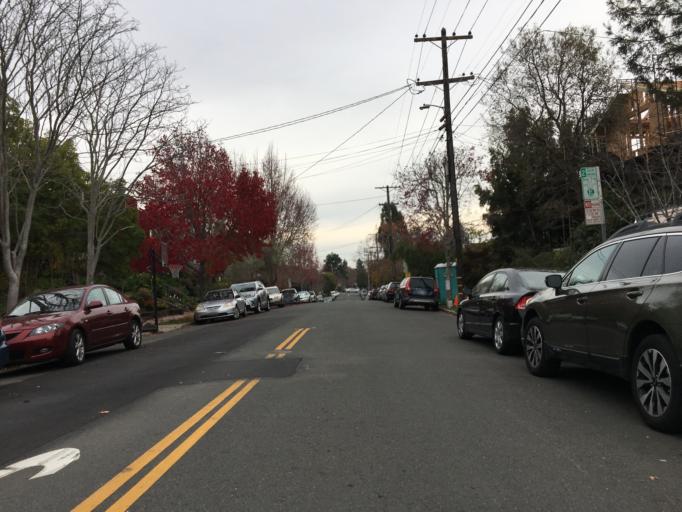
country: US
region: California
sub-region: Alameda County
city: Berkeley
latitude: 37.8795
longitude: -122.2751
